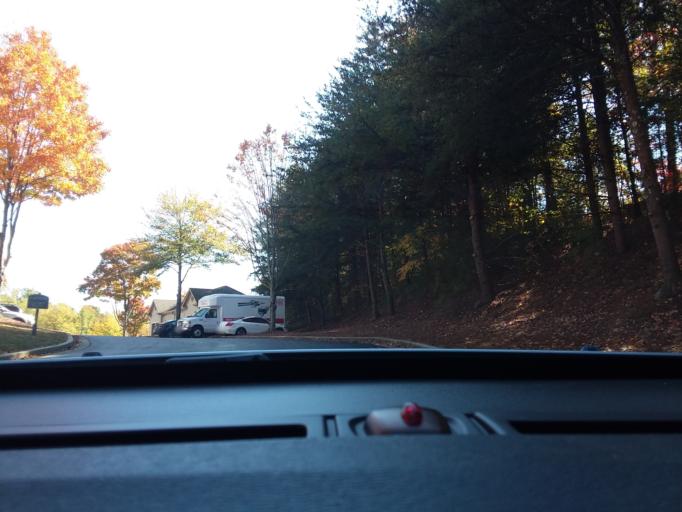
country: US
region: Georgia
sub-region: Fulton County
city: Johns Creek
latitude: 34.0275
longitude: -84.2483
